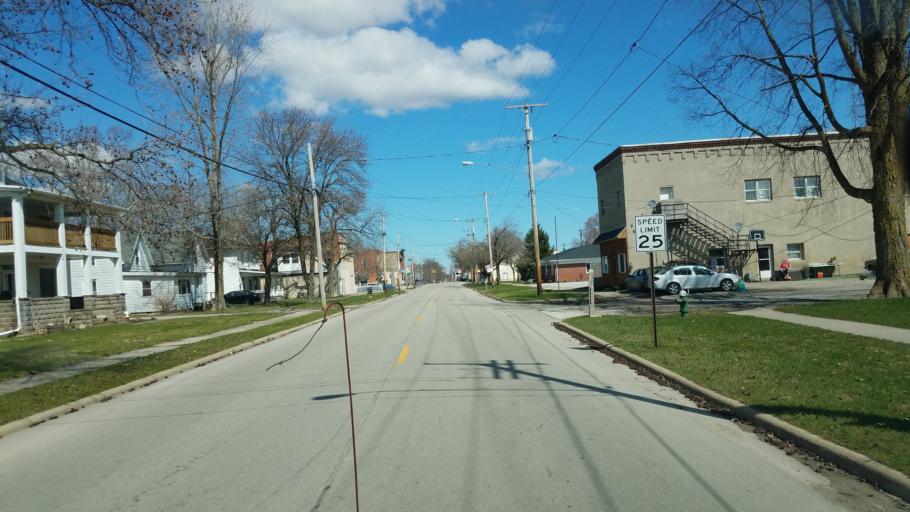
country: US
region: Ohio
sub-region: Sandusky County
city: Green Springs
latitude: 41.2539
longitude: -83.0521
